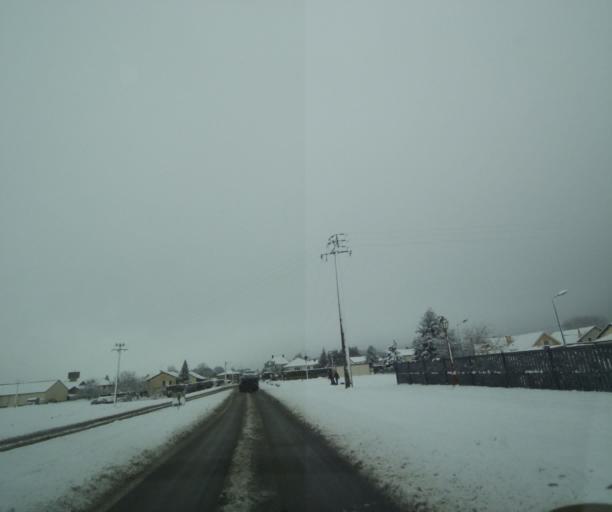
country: FR
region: Champagne-Ardenne
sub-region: Departement de la Haute-Marne
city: Saint-Dizier
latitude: 48.5801
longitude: 4.9054
